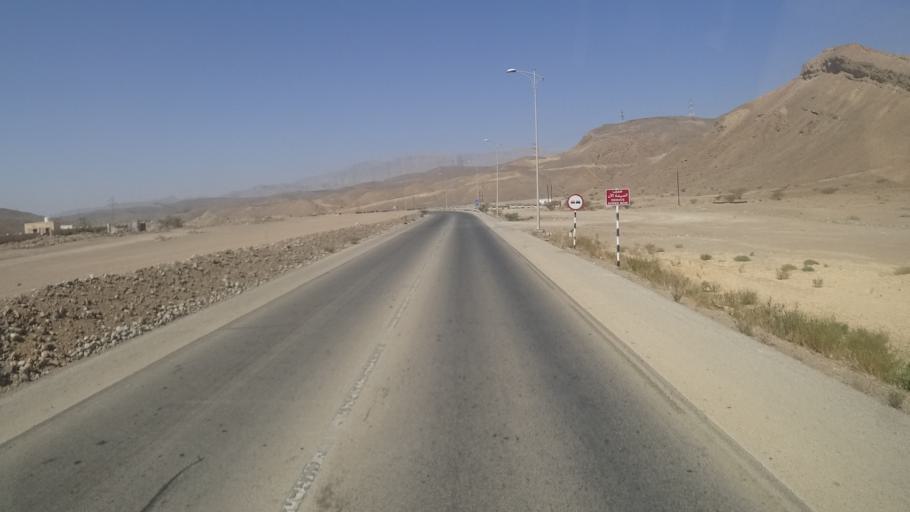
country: OM
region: Ash Sharqiyah
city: Sur
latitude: 22.5063
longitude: 59.4119
